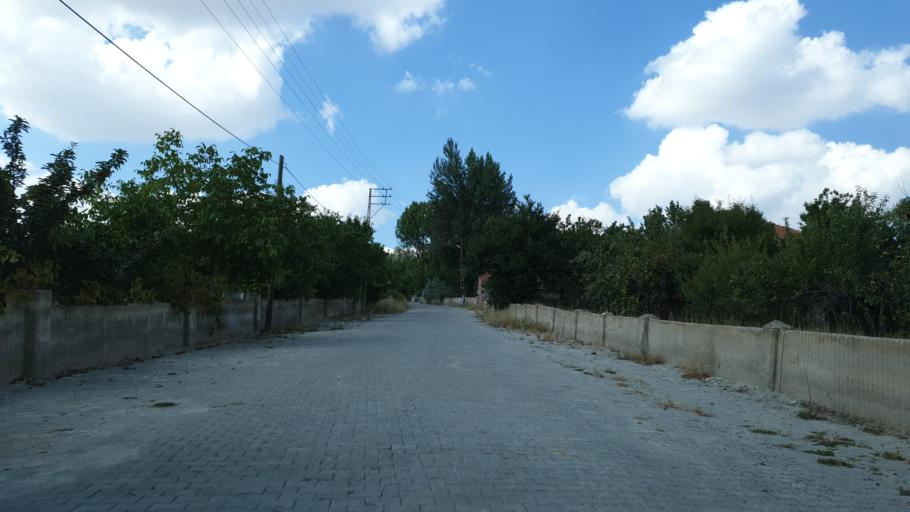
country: TR
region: Kayseri
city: Felahiye
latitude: 39.1140
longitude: 35.6103
